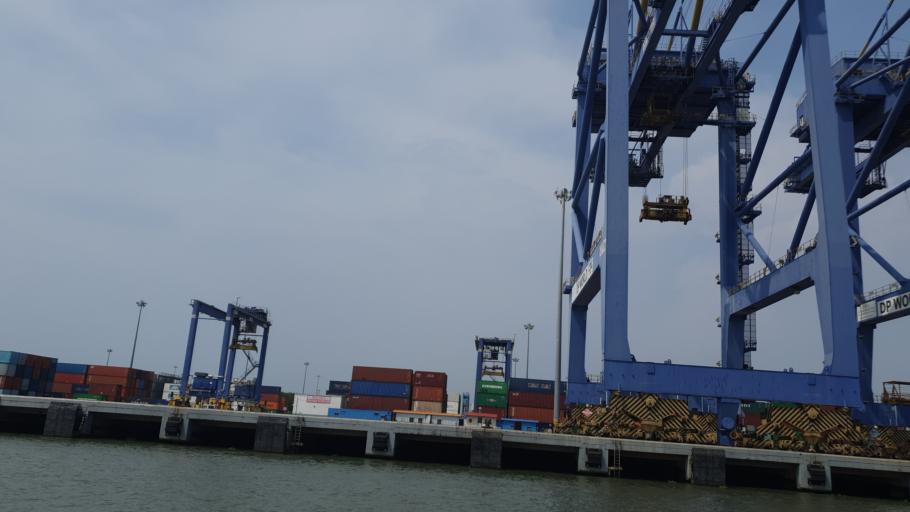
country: IN
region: Kerala
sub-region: Ernakulam
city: Cochin
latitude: 9.9774
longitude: 76.2529
